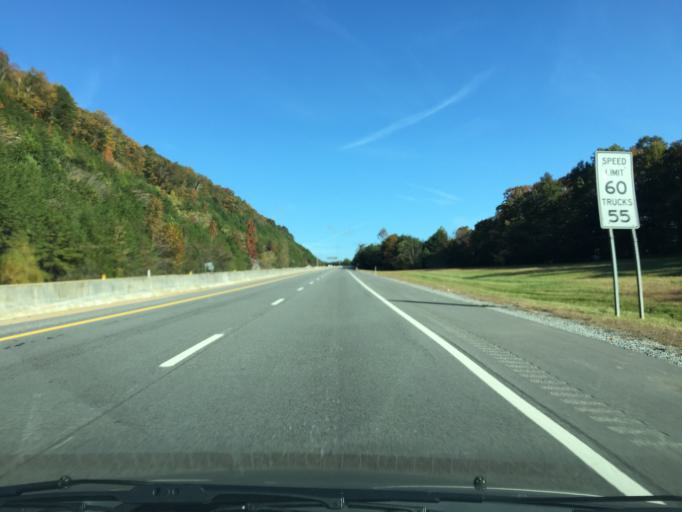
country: US
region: Tennessee
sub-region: Hamilton County
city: Soddy-Daisy
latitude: 35.3095
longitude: -85.1636
